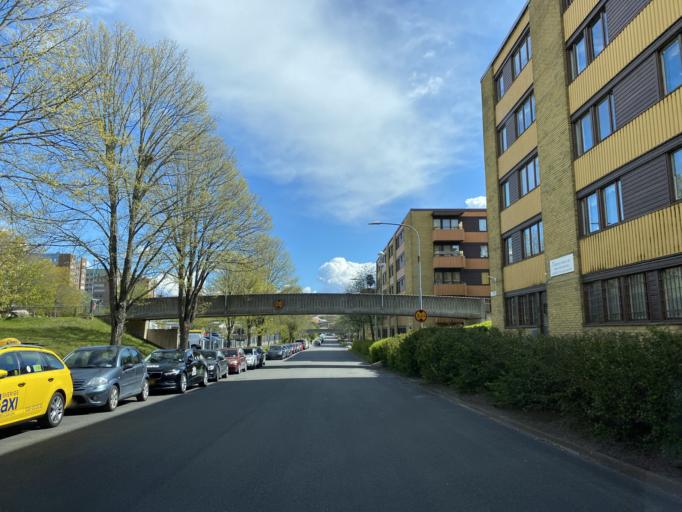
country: SE
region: Stockholm
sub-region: Stockholms Kommun
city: Kista
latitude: 59.4131
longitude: 17.9163
